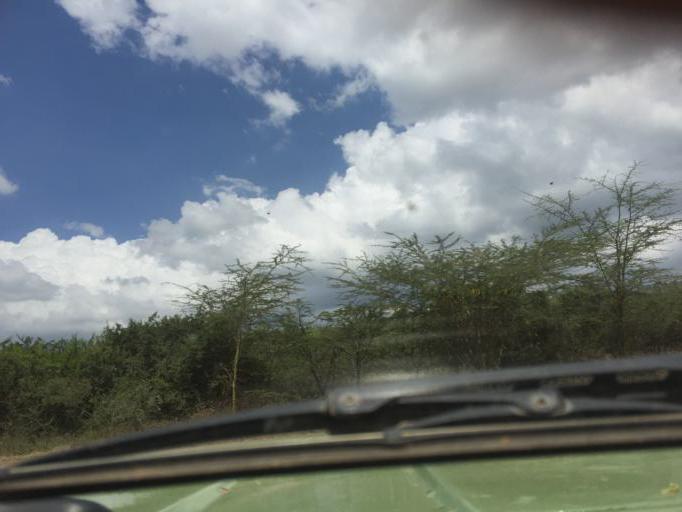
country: KE
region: Nyandarua
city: Ol Kalou
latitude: -0.3839
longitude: 36.2376
